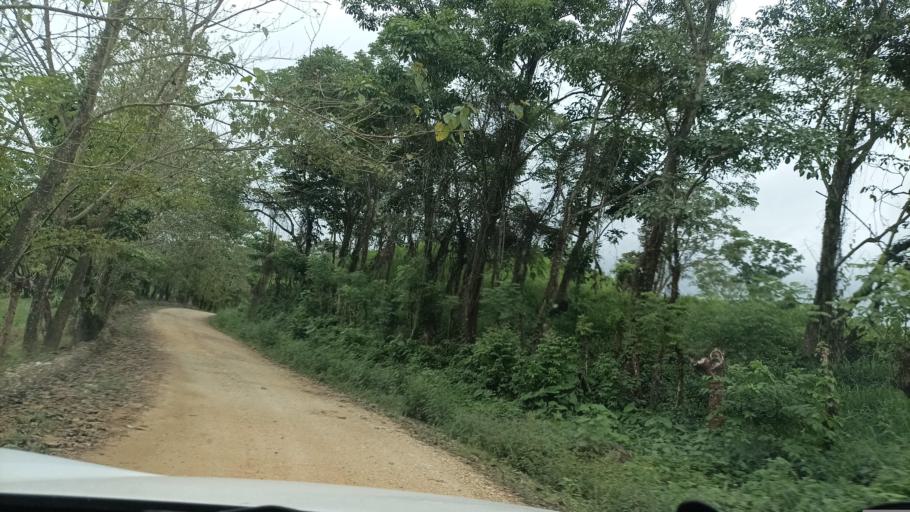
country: MX
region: Veracruz
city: Hidalgotitlan
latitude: 17.6293
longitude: -94.5111
